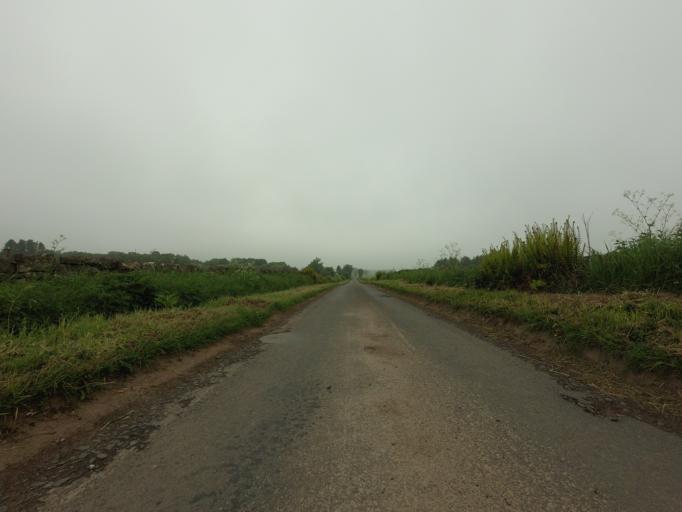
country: GB
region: Scotland
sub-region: Perth and Kinross
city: Abernethy
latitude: 56.2537
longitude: -3.3269
